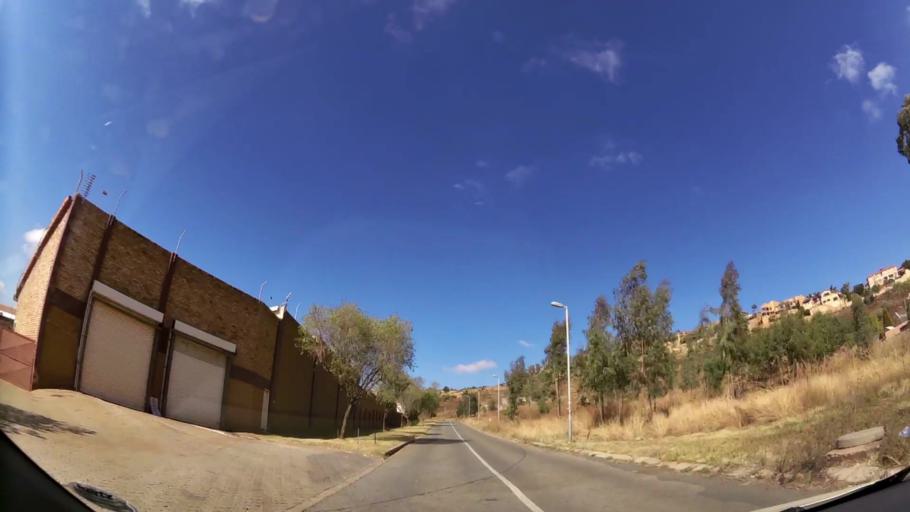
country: ZA
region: Gauteng
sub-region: West Rand District Municipality
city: Krugersdorp
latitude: -26.0932
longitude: 27.8254
